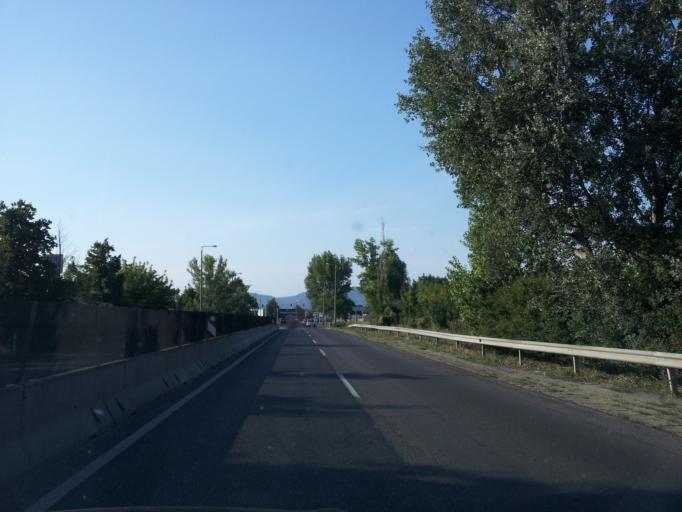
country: HU
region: Pest
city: Budakalasz
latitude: 47.6395
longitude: 19.0688
